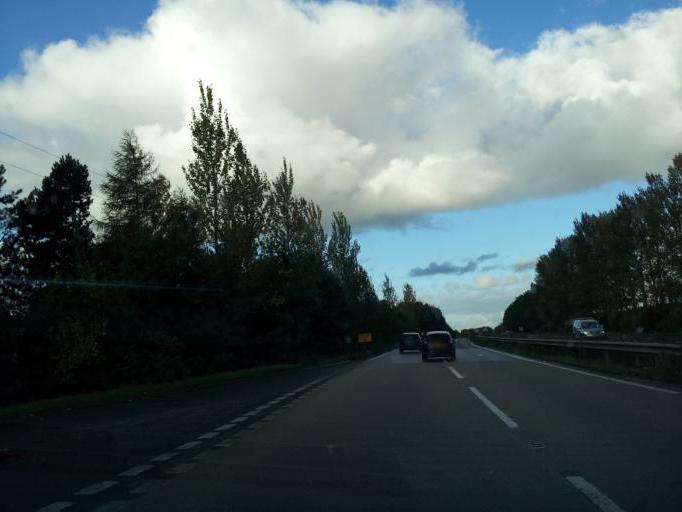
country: GB
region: England
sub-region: Norfolk
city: Brundall
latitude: 52.6366
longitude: 1.4601
